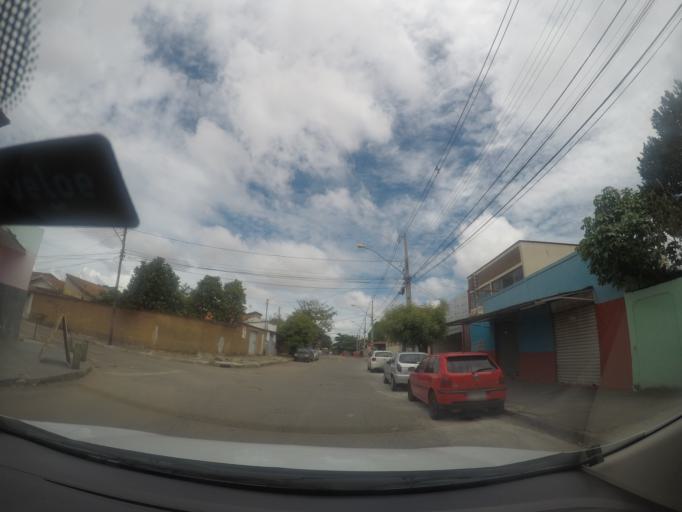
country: BR
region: Goias
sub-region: Goiania
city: Goiania
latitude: -16.6607
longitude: -49.3006
